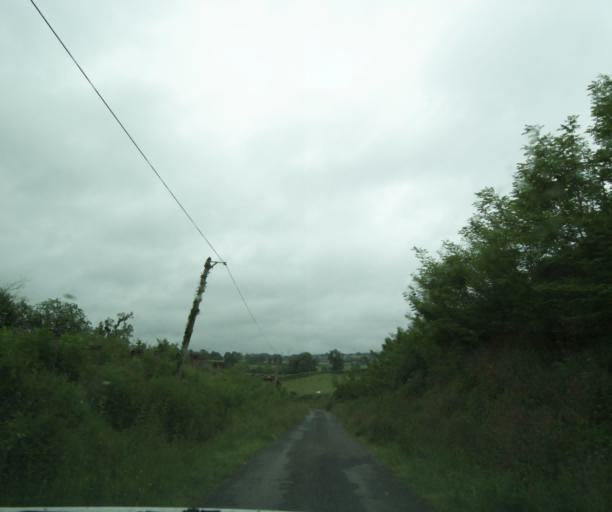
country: FR
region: Bourgogne
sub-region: Departement de Saone-et-Loire
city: Palinges
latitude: 46.4951
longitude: 4.2502
